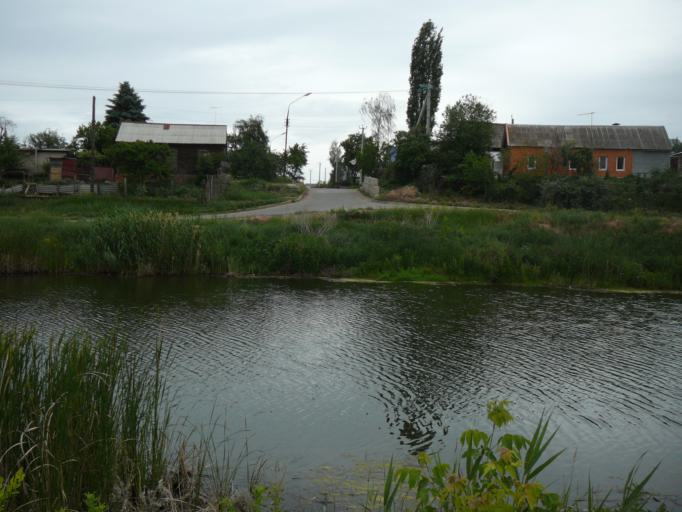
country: RU
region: Saratov
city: Engel's
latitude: 51.4742
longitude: 46.0940
